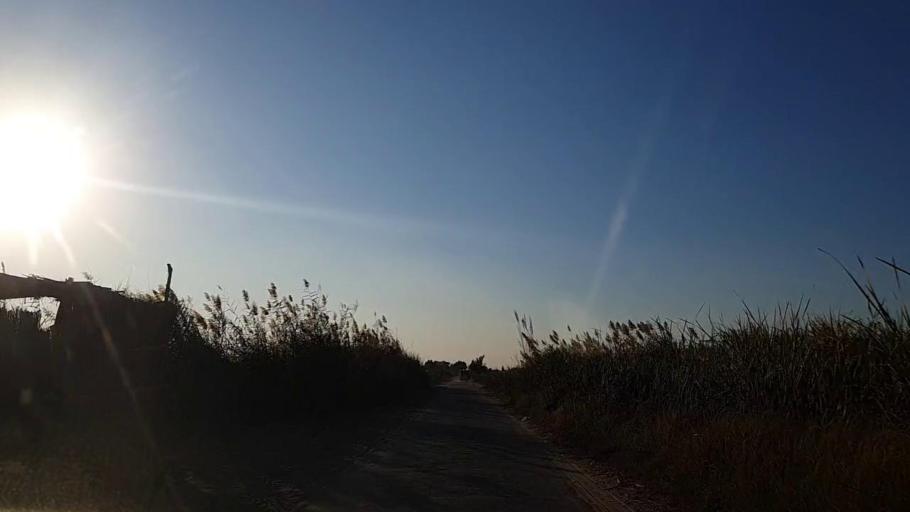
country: PK
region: Sindh
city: Khadro
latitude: 26.2790
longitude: 68.8372
